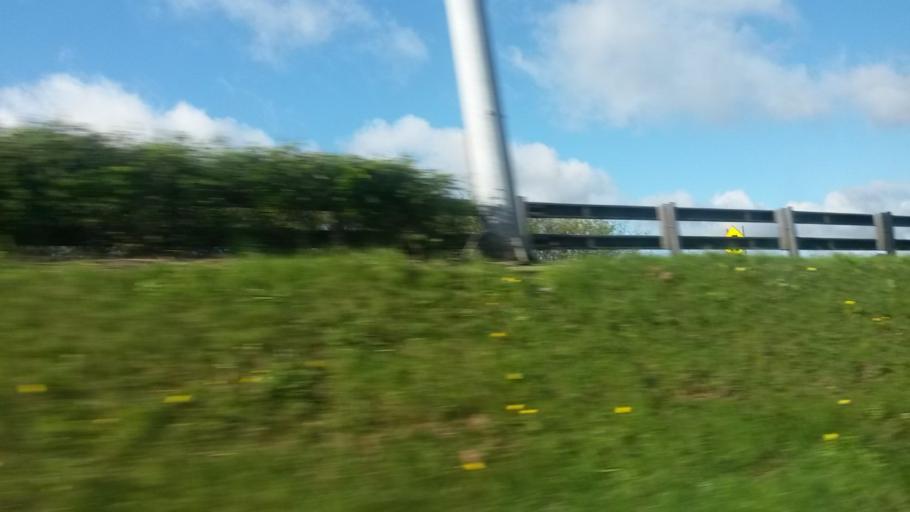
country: IE
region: Munster
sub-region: County Cork
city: Passage West
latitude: 51.9060
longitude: -8.3927
